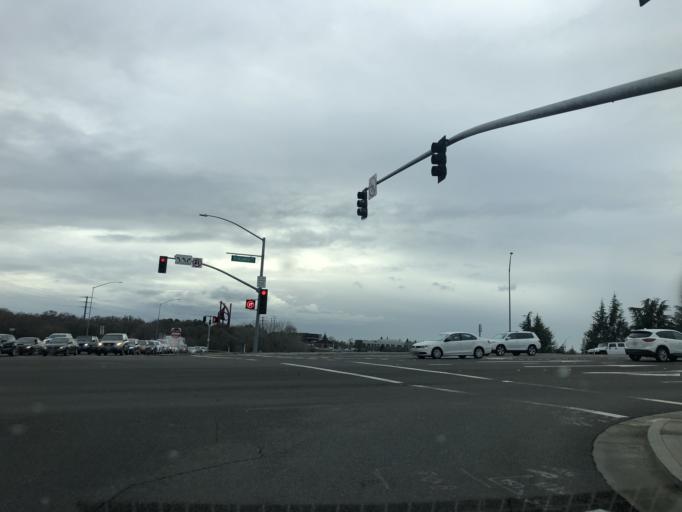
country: US
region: California
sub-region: Placer County
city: Roseville
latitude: 38.7578
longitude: -121.2595
